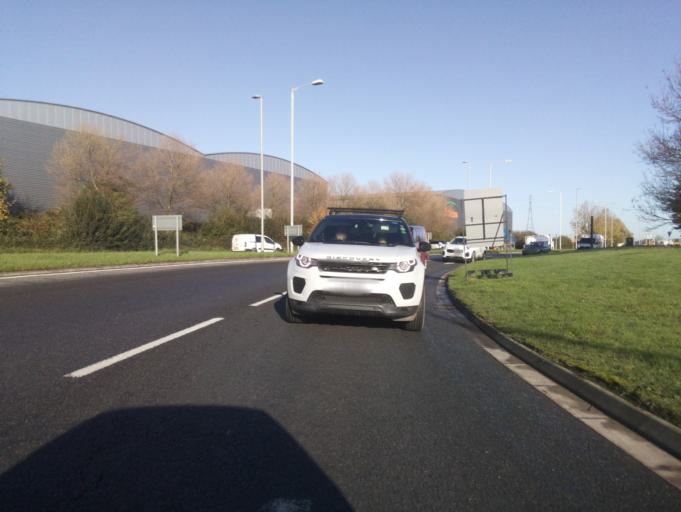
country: GB
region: England
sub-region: Somerset
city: Bridgwater
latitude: 51.1472
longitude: -2.9905
